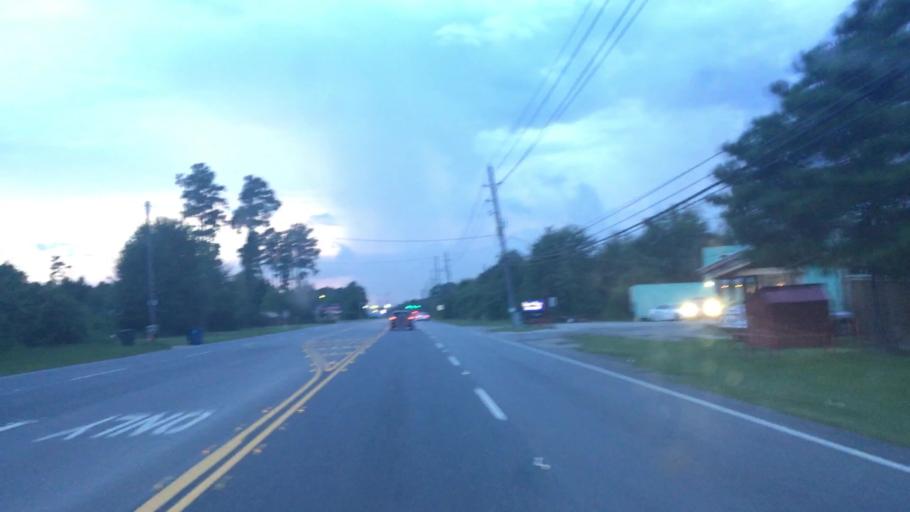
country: US
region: Texas
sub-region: Harris County
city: Humble
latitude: 29.9773
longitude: -95.2214
